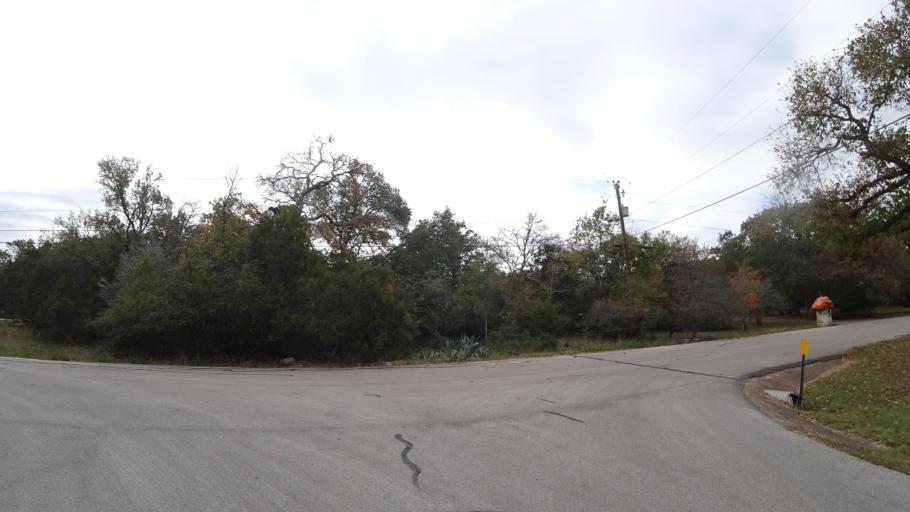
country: US
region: Texas
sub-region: Travis County
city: Shady Hollow
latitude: 30.1350
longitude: -97.8979
